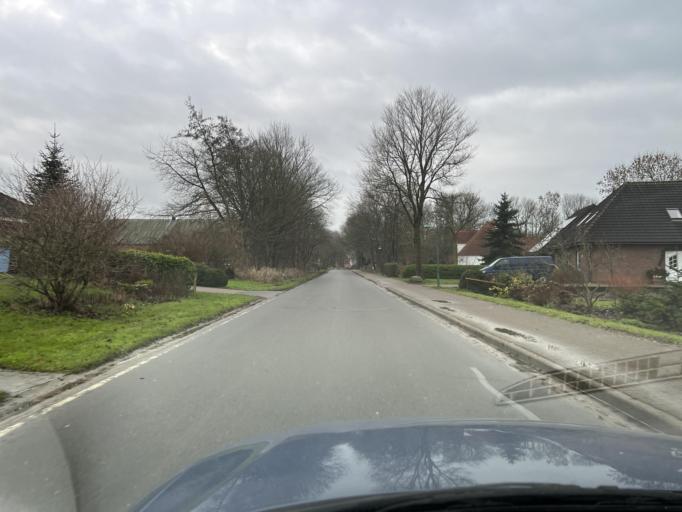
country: DE
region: Schleswig-Holstein
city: Norddeich
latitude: 54.2155
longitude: 8.8968
